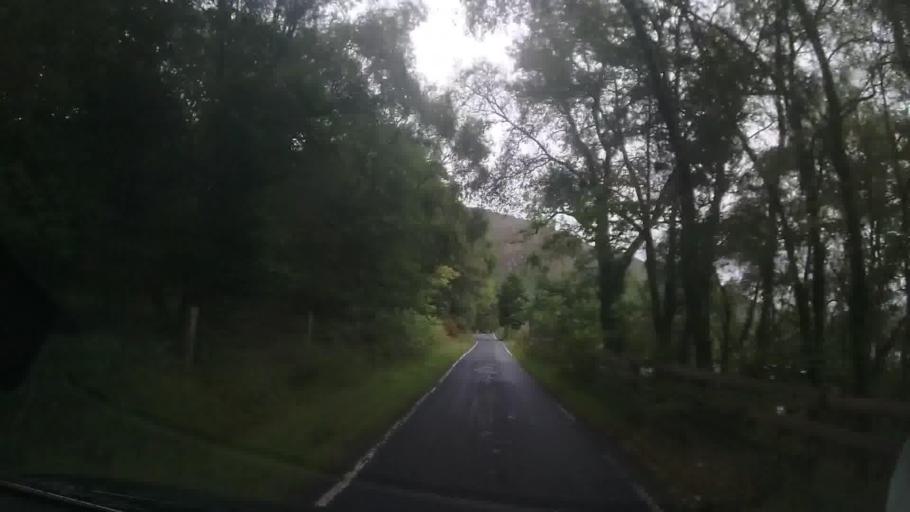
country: GB
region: Scotland
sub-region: Argyll and Bute
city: Isle Of Mull
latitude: 56.6794
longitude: -5.8695
